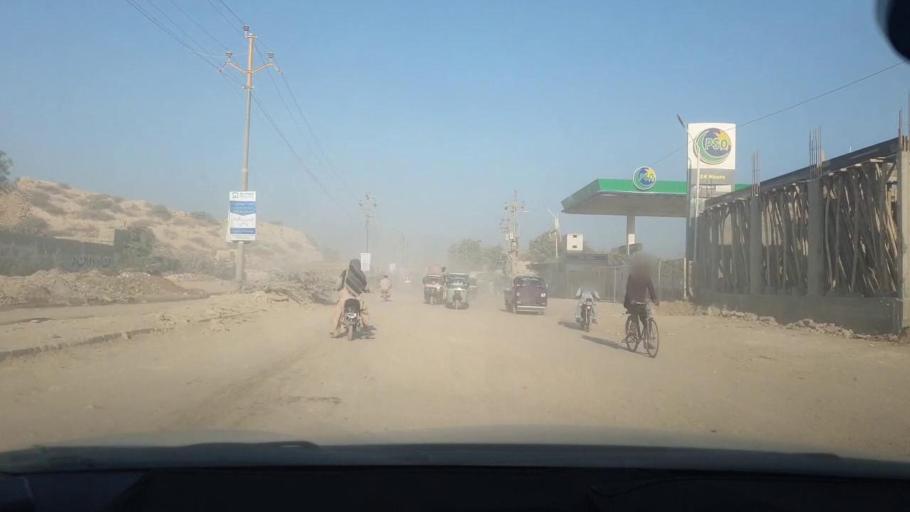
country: PK
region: Sindh
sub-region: Karachi District
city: Karachi
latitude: 24.9758
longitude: 67.0396
